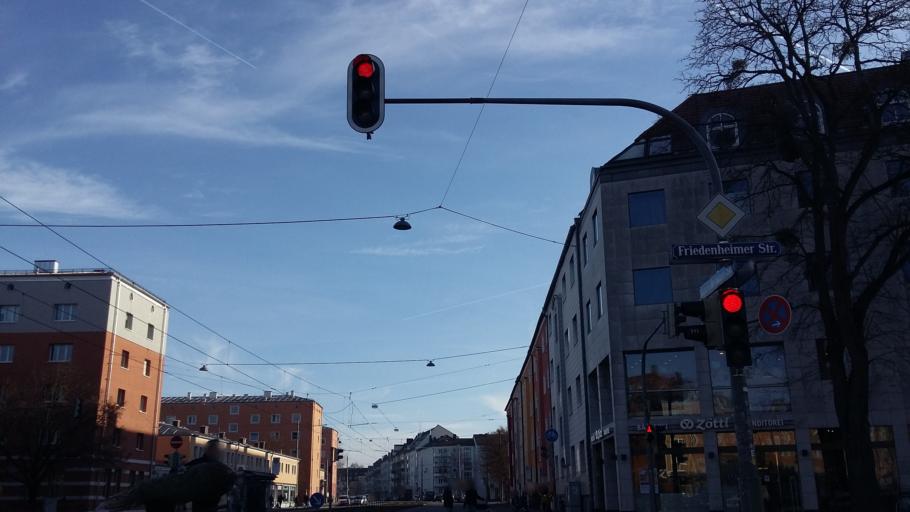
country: DE
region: Bavaria
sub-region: Upper Bavaria
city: Pasing
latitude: 48.1394
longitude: 11.5107
